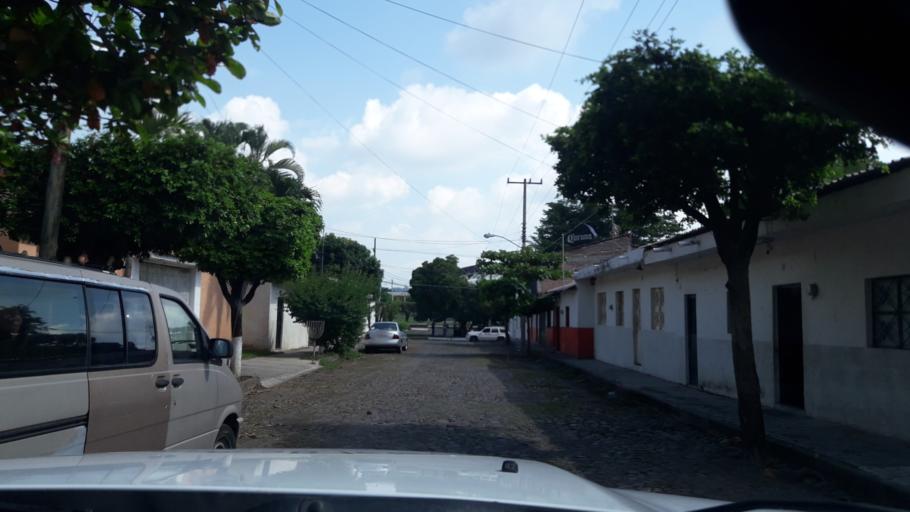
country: MX
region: Colima
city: Comala
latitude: 19.3298
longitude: -103.7536
